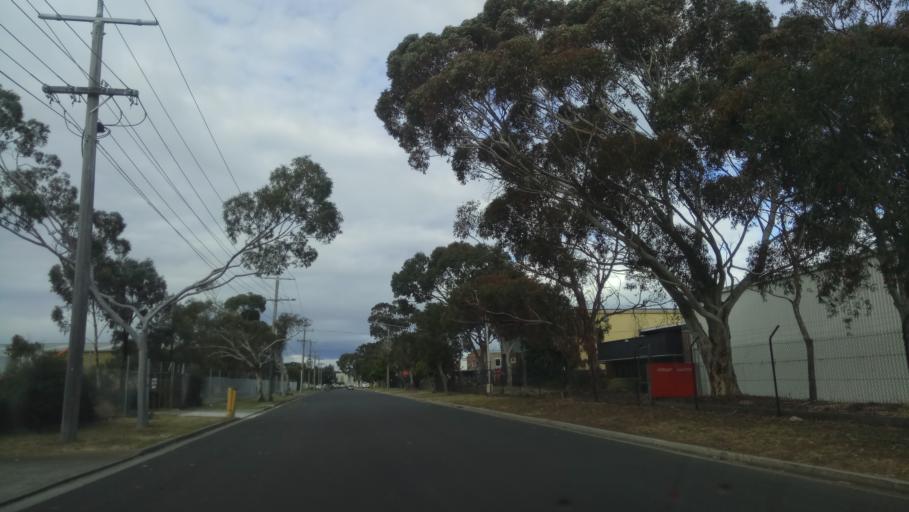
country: AU
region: Victoria
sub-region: Hobsons Bay
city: Altona
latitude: -37.8615
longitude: 144.8034
